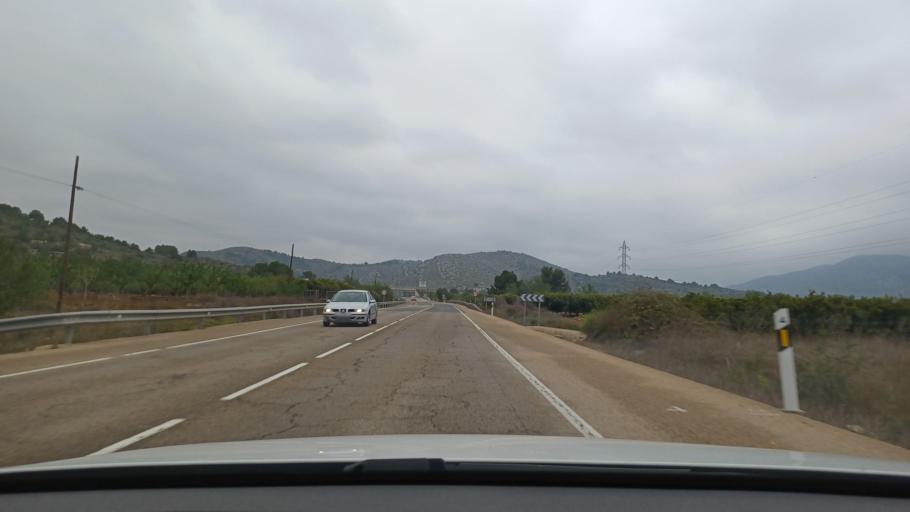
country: ES
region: Valencia
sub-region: Provincia de Castello
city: Alcala de Xivert
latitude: 40.2628
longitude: 0.2394
